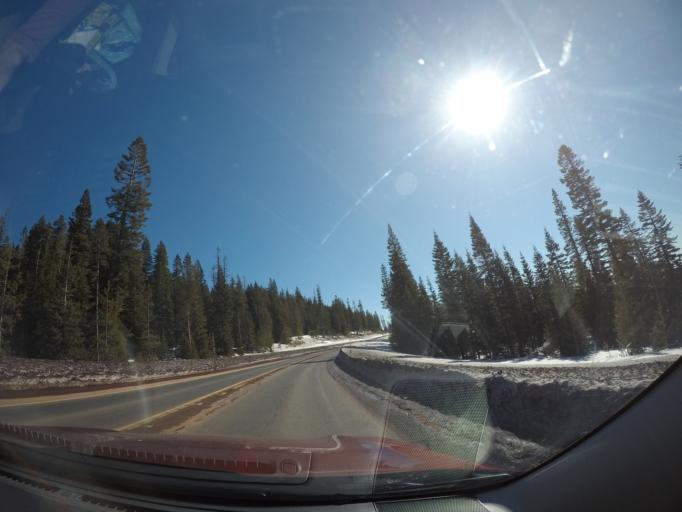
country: US
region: Oregon
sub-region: Deschutes County
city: Sunriver
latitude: 43.9826
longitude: -121.5922
